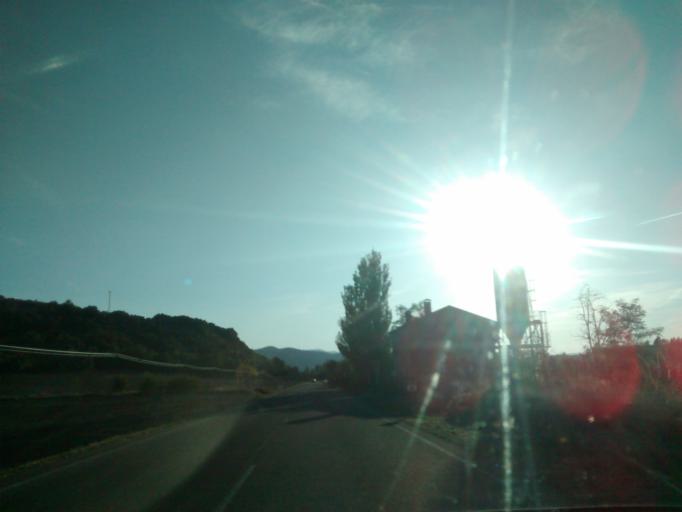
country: ES
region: Aragon
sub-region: Provincia de Huesca
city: Bailo
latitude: 42.5779
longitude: -0.7497
